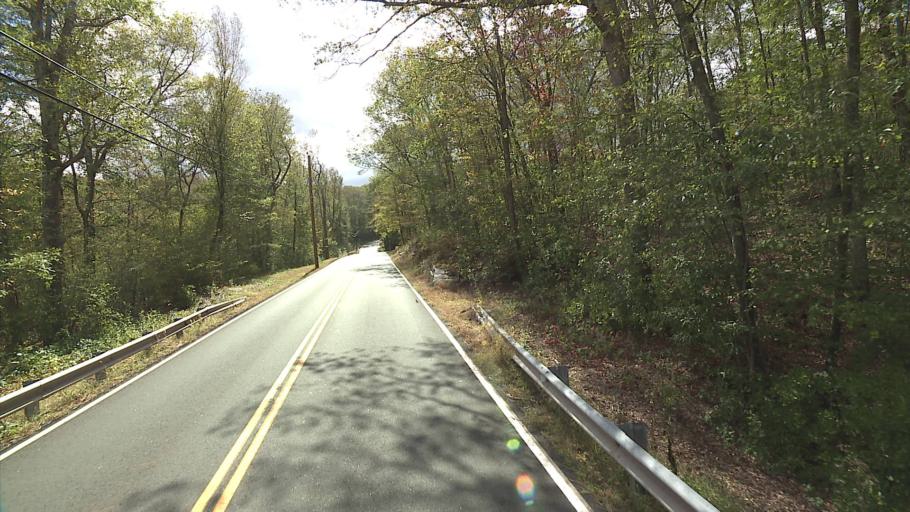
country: US
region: Connecticut
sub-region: Middlesex County
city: Higganum
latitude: 41.3997
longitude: -72.6046
